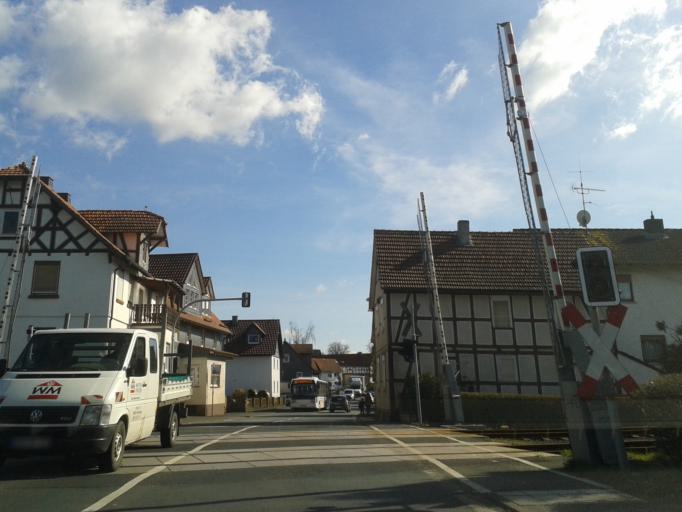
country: DE
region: Hesse
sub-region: Regierungsbezirk Giessen
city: Munchhausen
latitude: 50.9633
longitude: 8.7160
